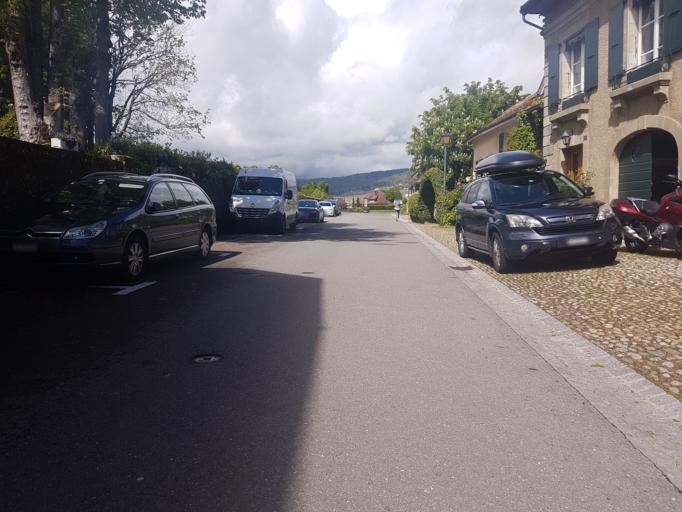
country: CH
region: Vaud
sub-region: Nyon District
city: Perroy
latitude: 46.4678
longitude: 6.3640
